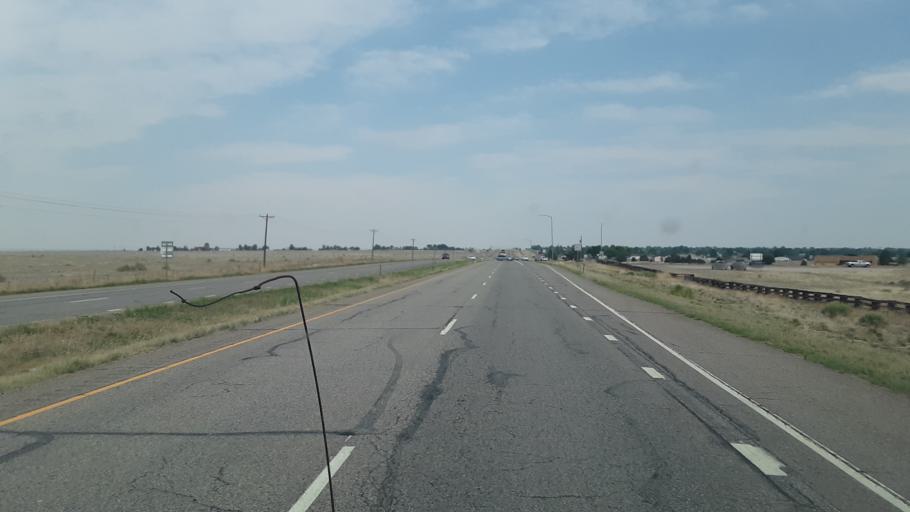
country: US
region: Colorado
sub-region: Pueblo County
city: Pueblo West
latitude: 38.3432
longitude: -104.7717
